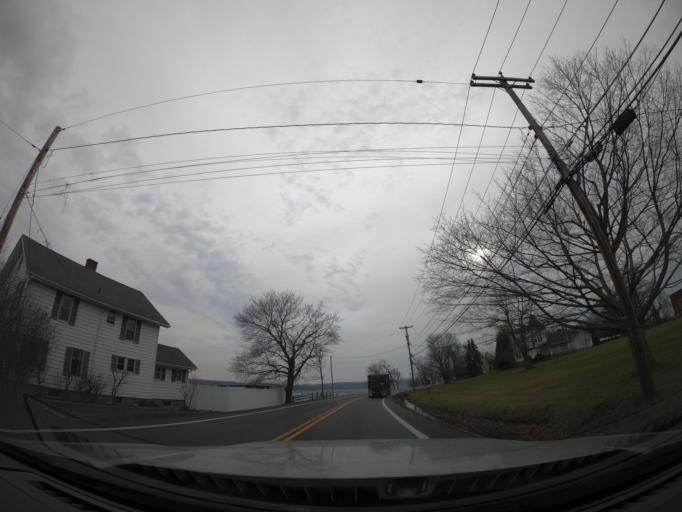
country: US
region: New York
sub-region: Cayuga County
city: Melrose Park
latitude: 42.8709
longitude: -76.5360
